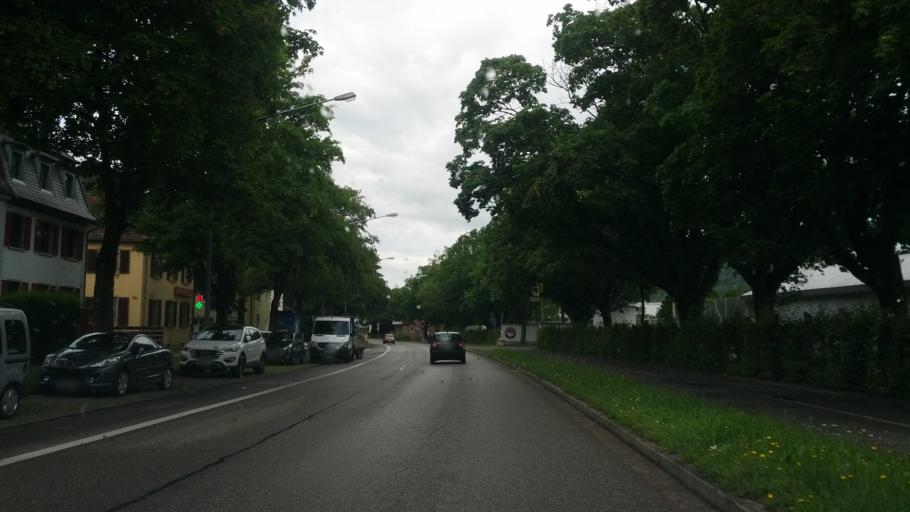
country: DE
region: Baden-Wuerttemberg
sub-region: Freiburg Region
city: Freiburg
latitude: 47.9888
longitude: 7.8844
